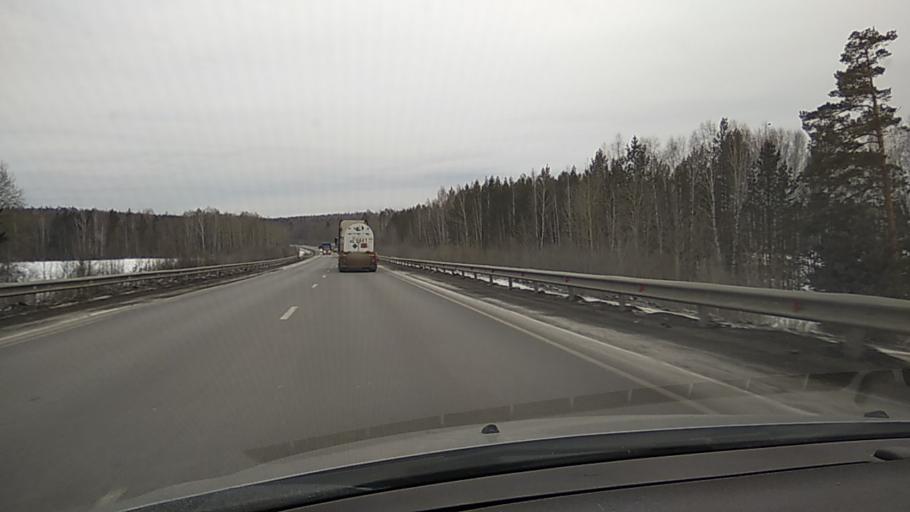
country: RU
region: Sverdlovsk
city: Talitsa
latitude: 56.8454
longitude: 60.0231
